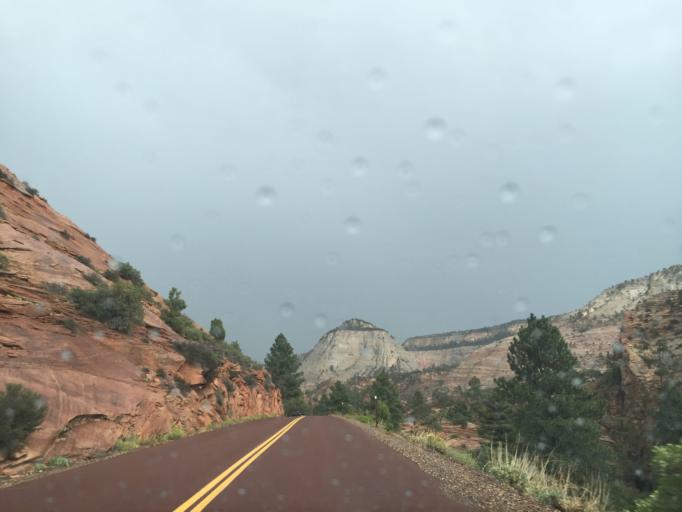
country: US
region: Utah
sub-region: Washington County
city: Hildale
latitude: 37.2236
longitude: -112.9135
